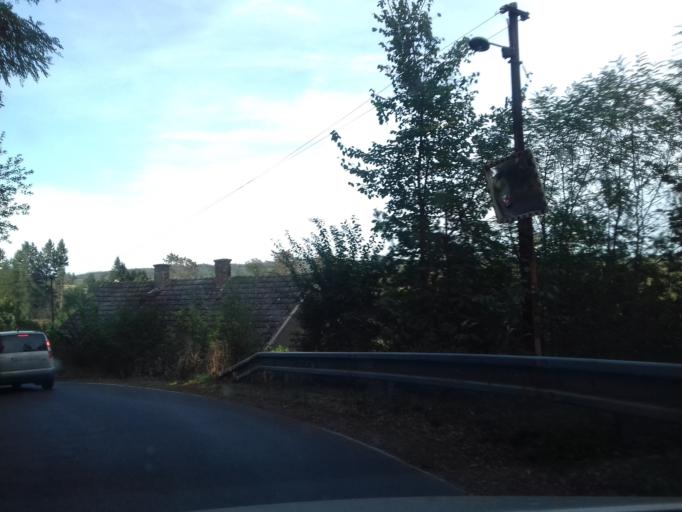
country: CZ
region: Central Bohemia
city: Kamenny Privoz
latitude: 49.8582
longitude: 14.5066
